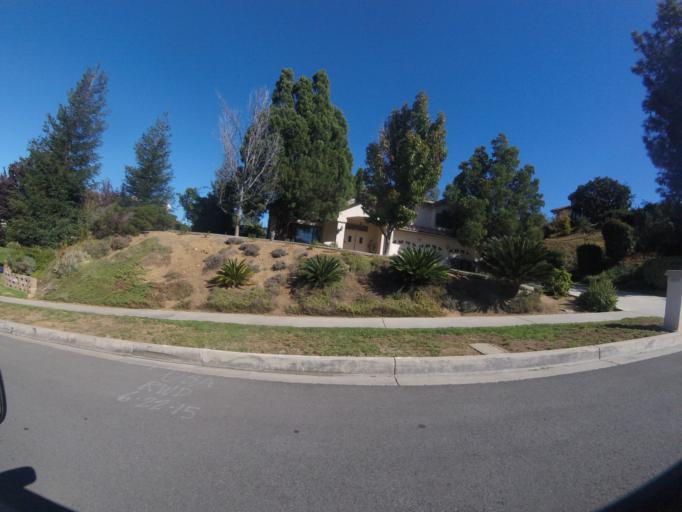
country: US
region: California
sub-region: San Bernardino County
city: Mentone
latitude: 34.0246
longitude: -117.1351
